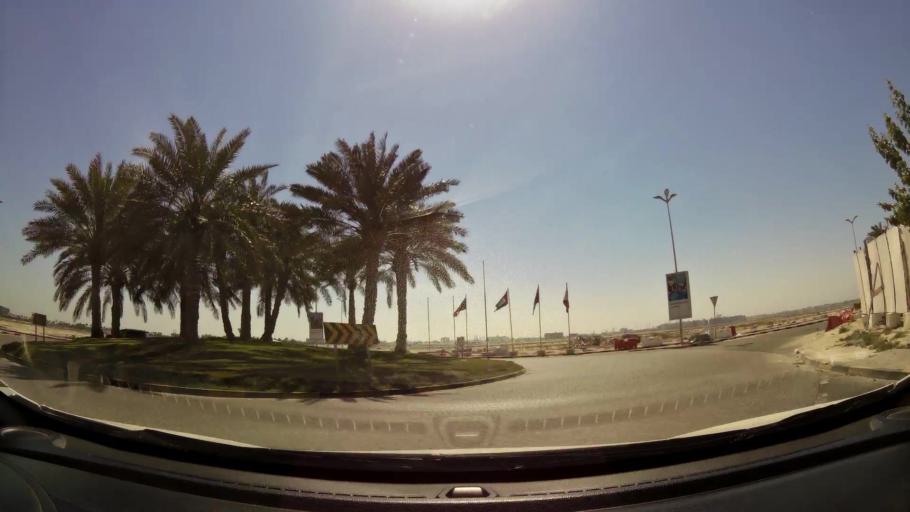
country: BH
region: Muharraq
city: Al Hadd
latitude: 26.2873
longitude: 50.6601
